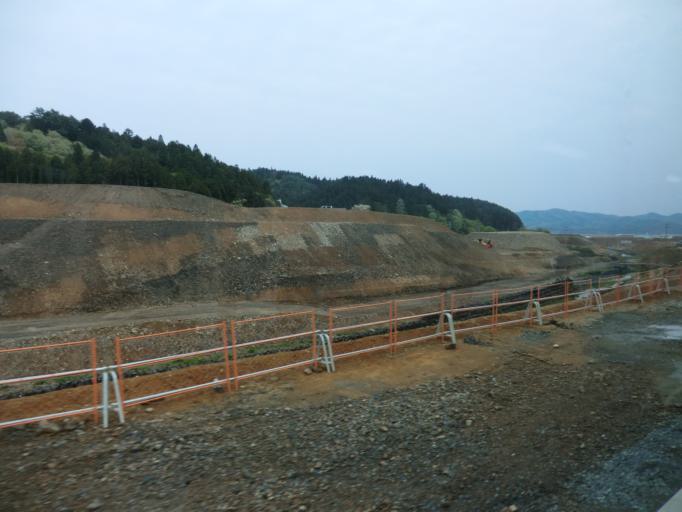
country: JP
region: Miyagi
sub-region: Oshika Gun
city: Onagawa Cho
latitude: 38.6830
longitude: 141.4517
